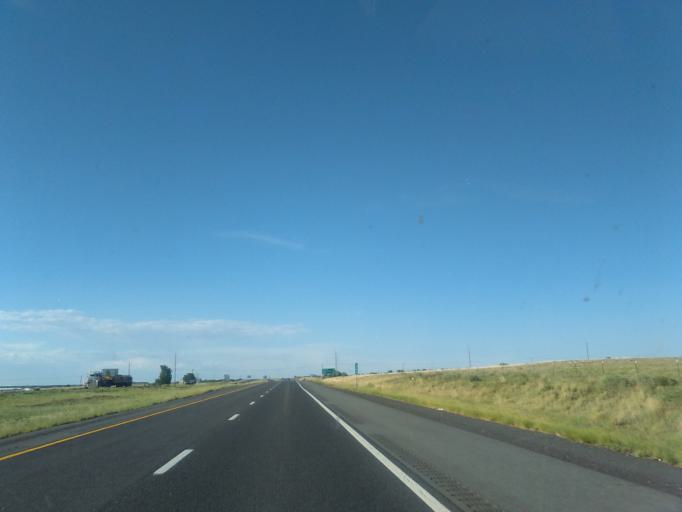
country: US
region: New Mexico
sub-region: San Miguel County
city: Las Vegas
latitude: 35.6369
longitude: -105.1985
